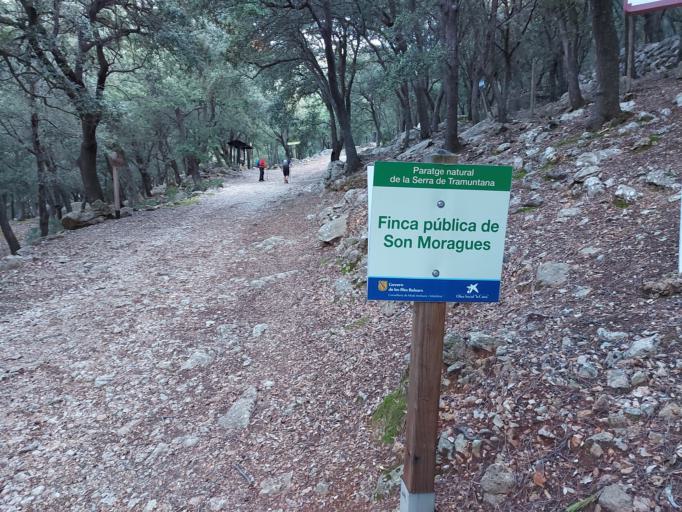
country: ES
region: Balearic Islands
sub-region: Illes Balears
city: Valldemossa
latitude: 39.7200
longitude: 2.6456
